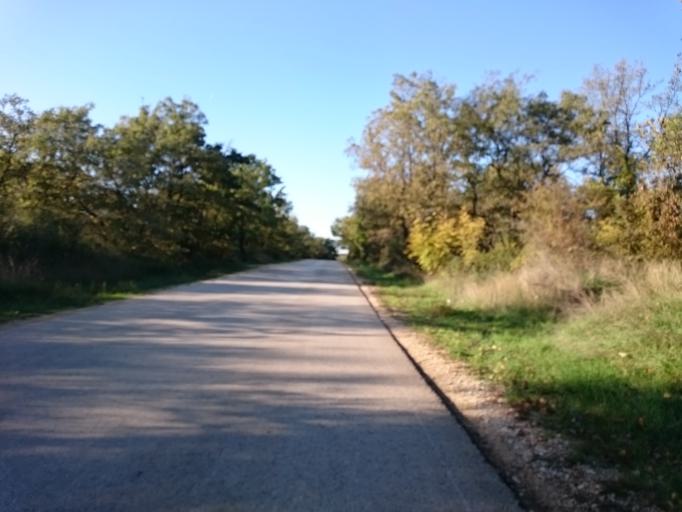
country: HR
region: Istarska
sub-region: Grad Porec
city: Porec
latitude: 45.2835
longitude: 13.6443
